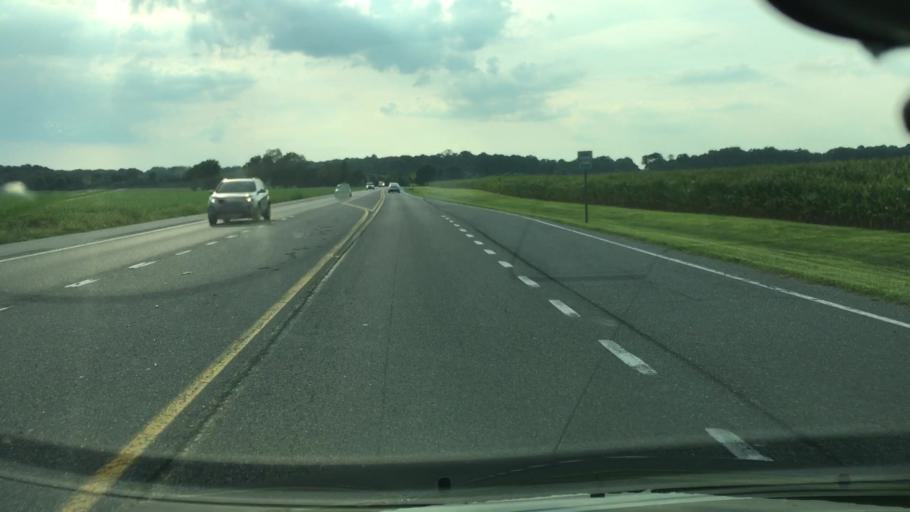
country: US
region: Maryland
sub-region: Worcester County
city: Ocean Pines
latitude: 38.3871
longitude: -75.1966
